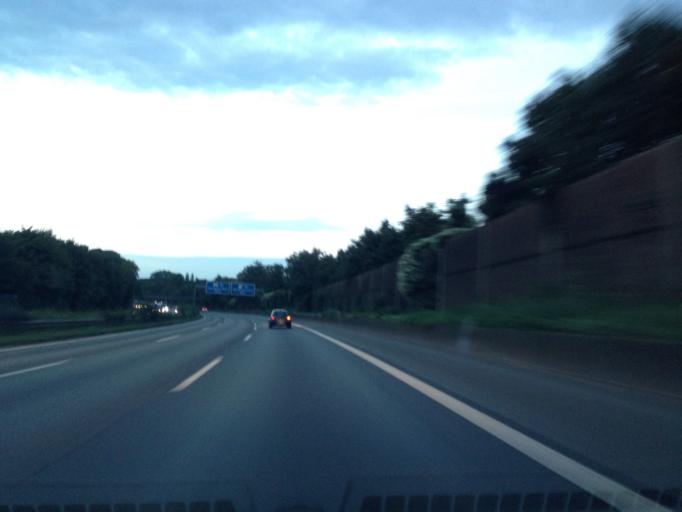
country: DE
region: North Rhine-Westphalia
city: Meiderich
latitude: 51.4639
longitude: 6.8149
